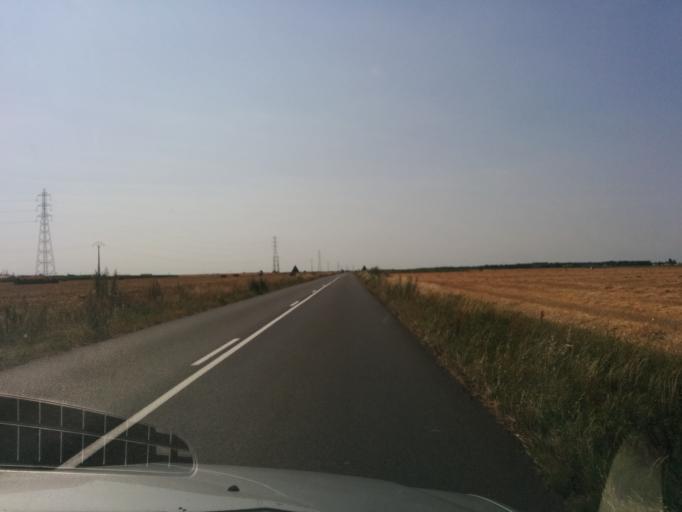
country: FR
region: Poitou-Charentes
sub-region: Departement des Deux-Sevres
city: Airvault
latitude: 46.8141
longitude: -0.0798
